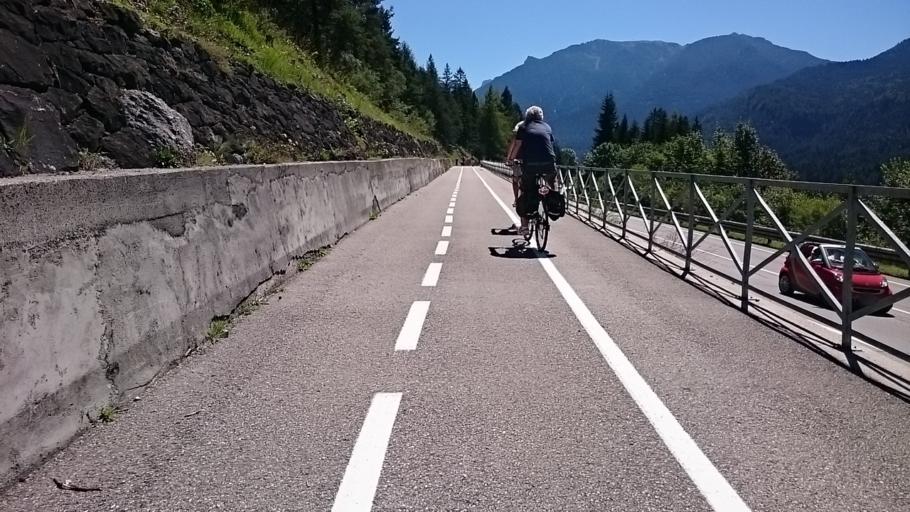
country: IT
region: Veneto
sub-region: Provincia di Belluno
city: Borca
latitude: 46.4428
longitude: 12.2142
